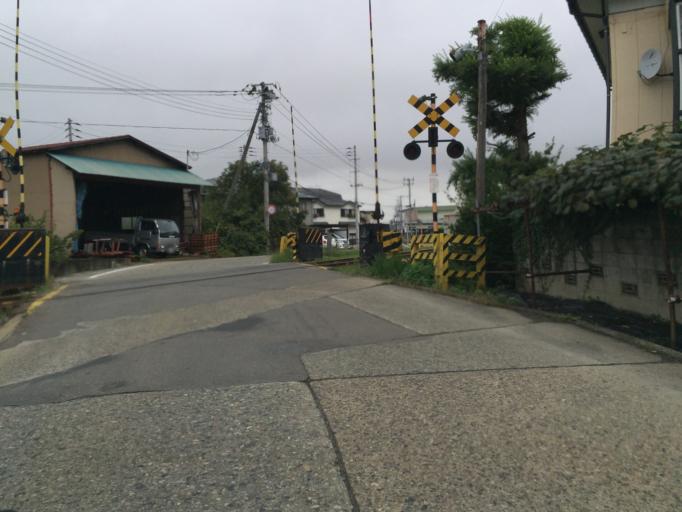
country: JP
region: Fukushima
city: Kitakata
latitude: 37.4718
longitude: 139.9132
